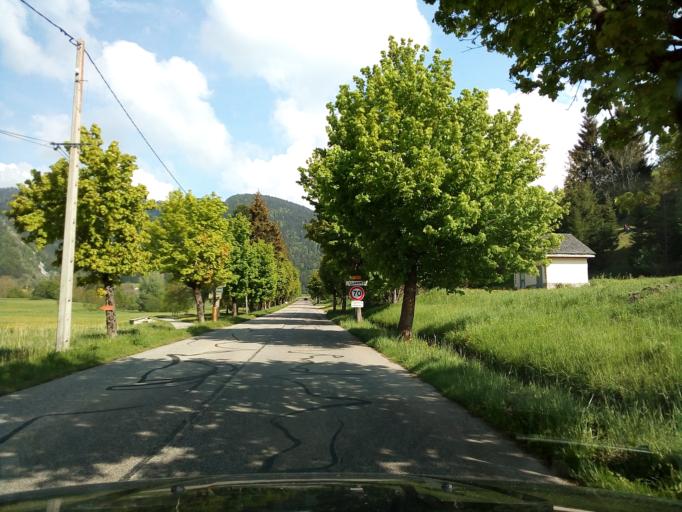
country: FR
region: Rhone-Alpes
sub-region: Departement de l'Isere
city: Autrans
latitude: 45.1727
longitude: 5.5469
